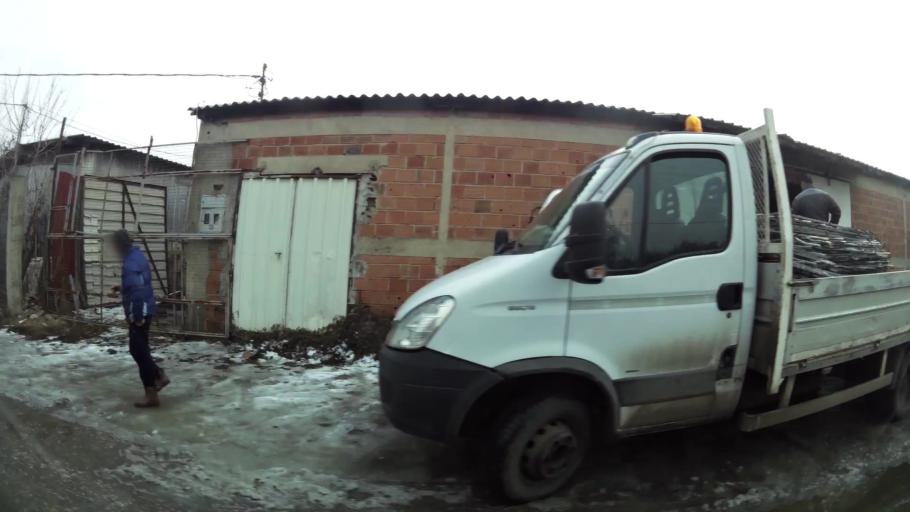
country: MK
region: Kisela Voda
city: Kisela Voda
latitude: 41.9947
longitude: 21.5003
